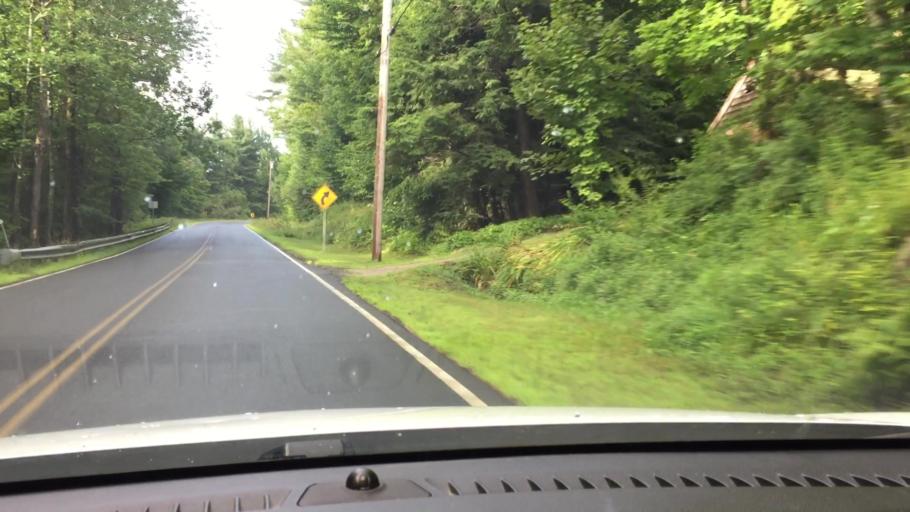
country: US
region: Massachusetts
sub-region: Berkshire County
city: Becket
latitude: 42.4257
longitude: -72.9982
